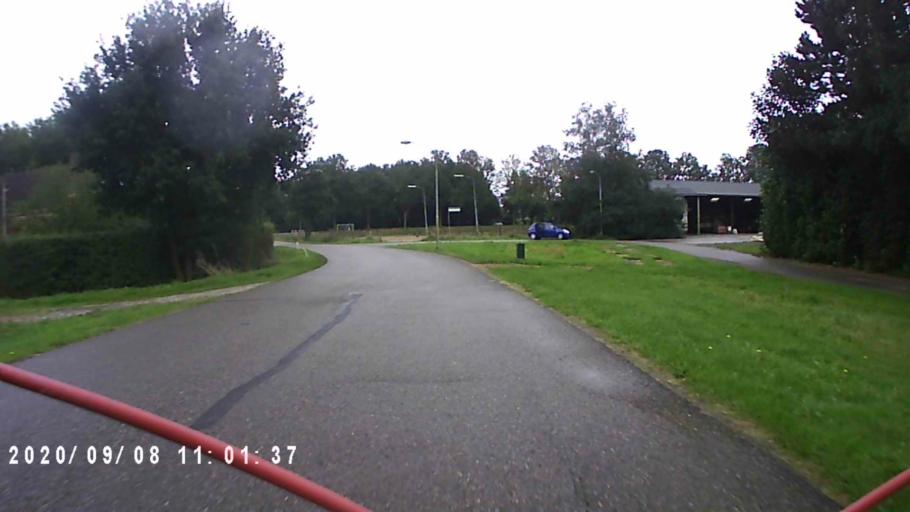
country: NL
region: Groningen
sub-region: Gemeente Haren
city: Haren
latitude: 53.1981
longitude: 6.6647
